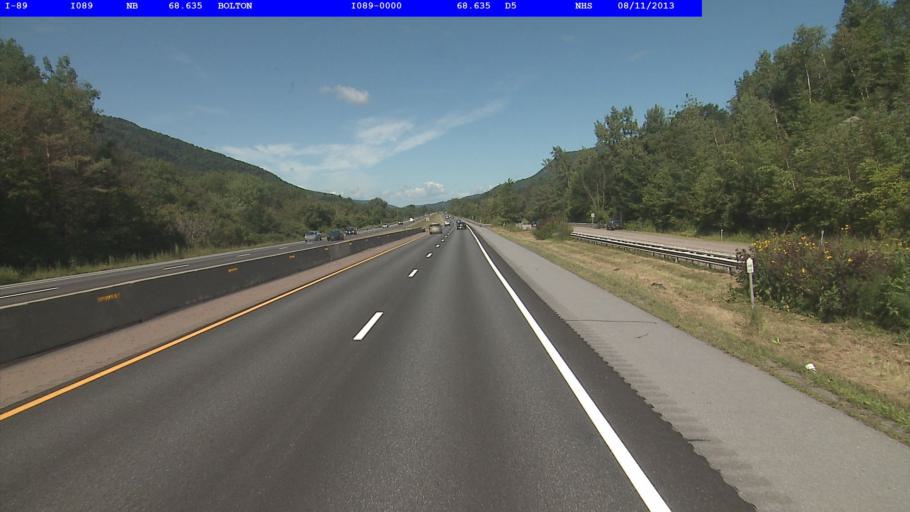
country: US
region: Vermont
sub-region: Washington County
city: Waterbury
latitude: 44.3631
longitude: -72.8423
